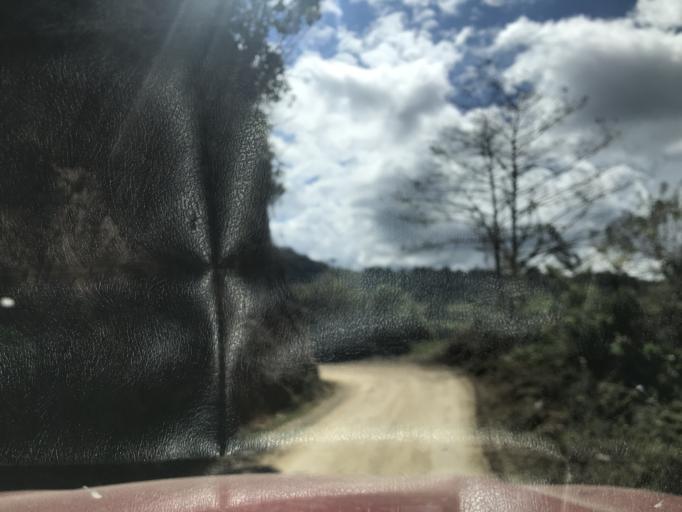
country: PE
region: Cajamarca
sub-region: Provincia de Chota
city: Querocoto
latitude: -6.3506
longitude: -79.0430
